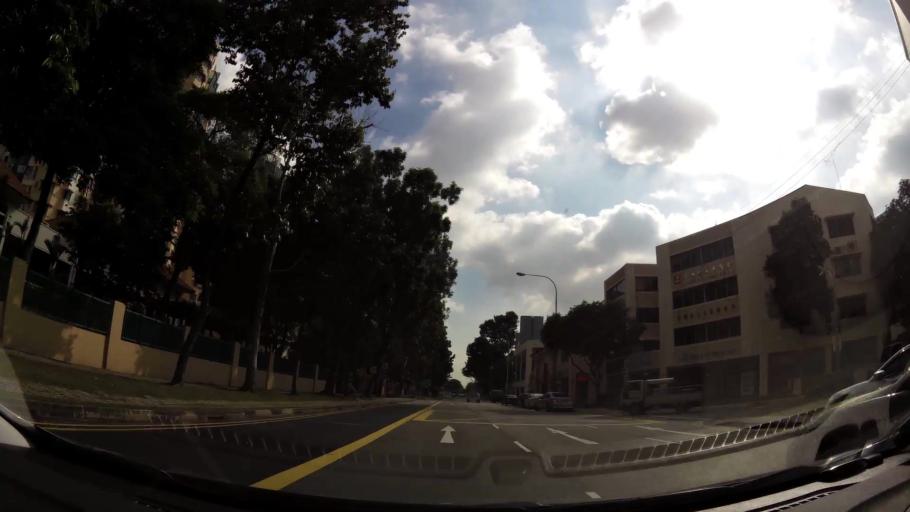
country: SG
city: Singapore
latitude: 1.3164
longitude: 103.8897
